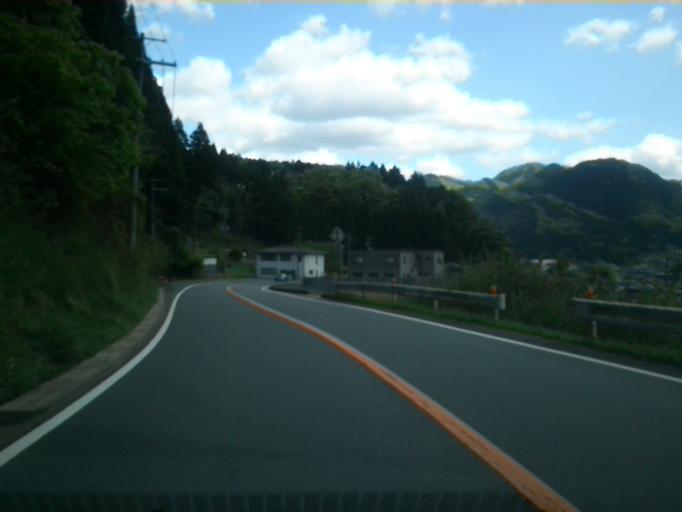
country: JP
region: Kyoto
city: Fukuchiyama
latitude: 35.3384
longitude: 135.0688
